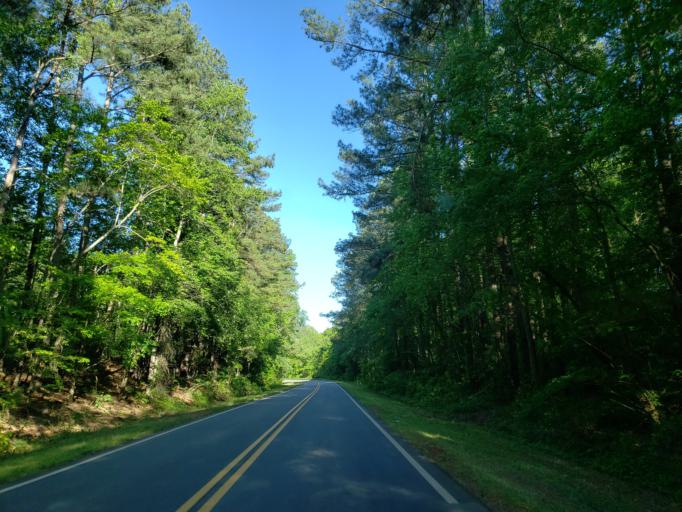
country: US
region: Georgia
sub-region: Haralson County
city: Tallapoosa
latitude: 33.7946
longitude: -85.2663
